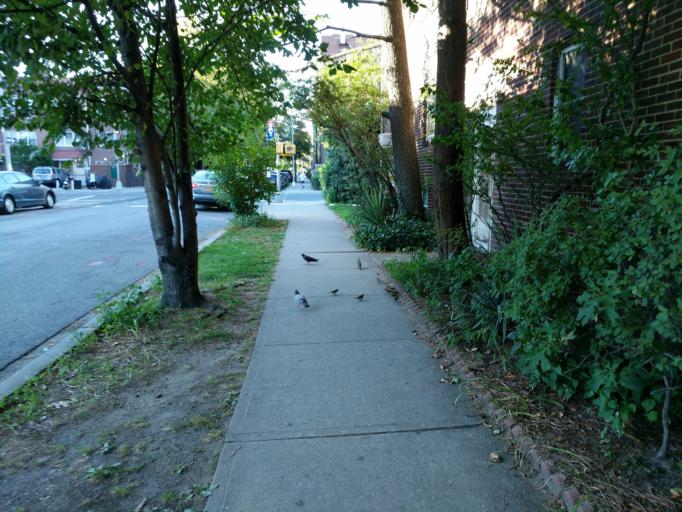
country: US
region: New York
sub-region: Queens County
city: Long Island City
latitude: 40.7551
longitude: -73.9070
